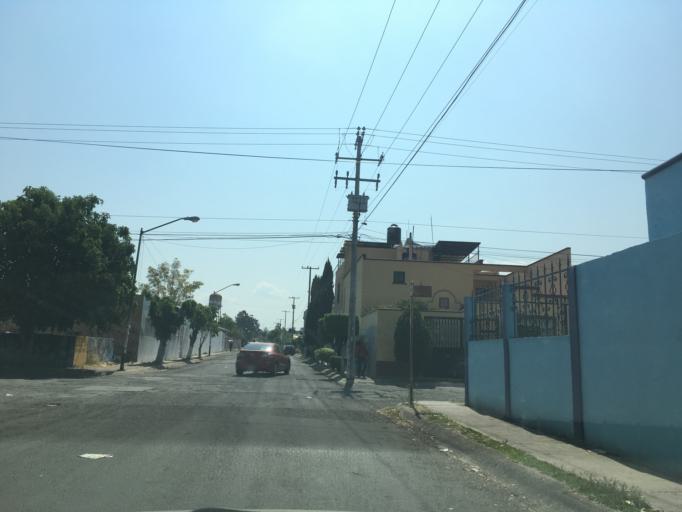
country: MX
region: Michoacan
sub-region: Morelia
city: Morelos
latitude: 19.6740
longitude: -101.2282
